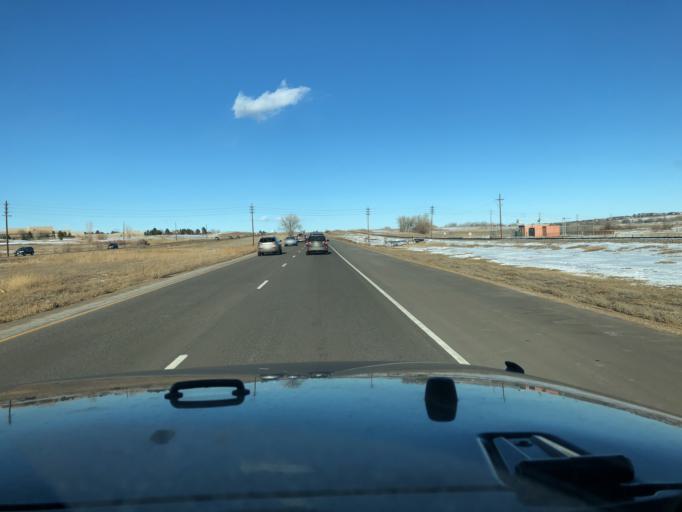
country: US
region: Colorado
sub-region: Boulder County
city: Gunbarrel
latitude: 40.0784
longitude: -105.2020
